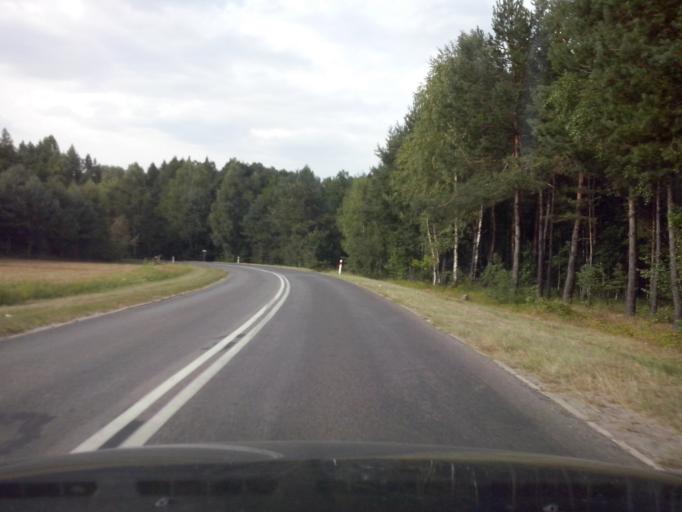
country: PL
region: Swietokrzyskie
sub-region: Powiat kielecki
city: Rakow
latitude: 50.6553
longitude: 21.0719
